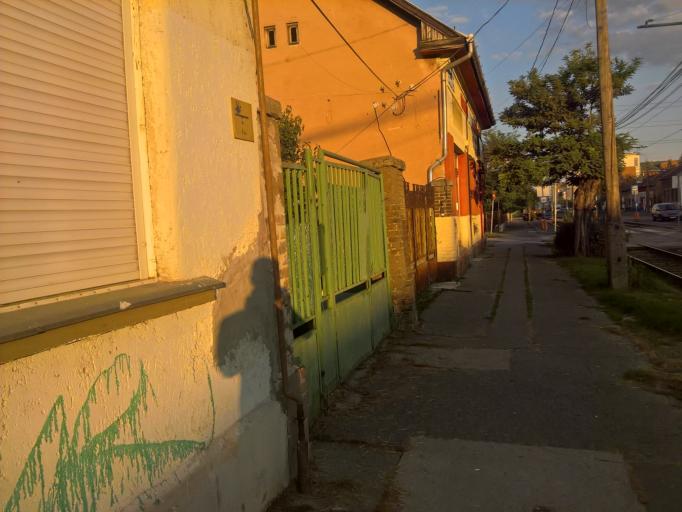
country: HU
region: Budapest
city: Budapest XIX. keruelet
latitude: 47.4501
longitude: 19.1626
